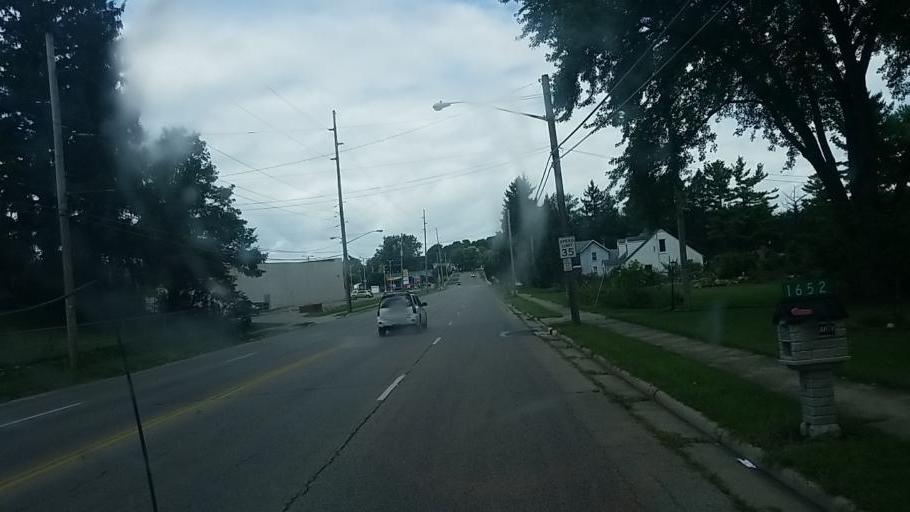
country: US
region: Ohio
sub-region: Clark County
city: Springfield
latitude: 39.9026
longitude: -83.7913
